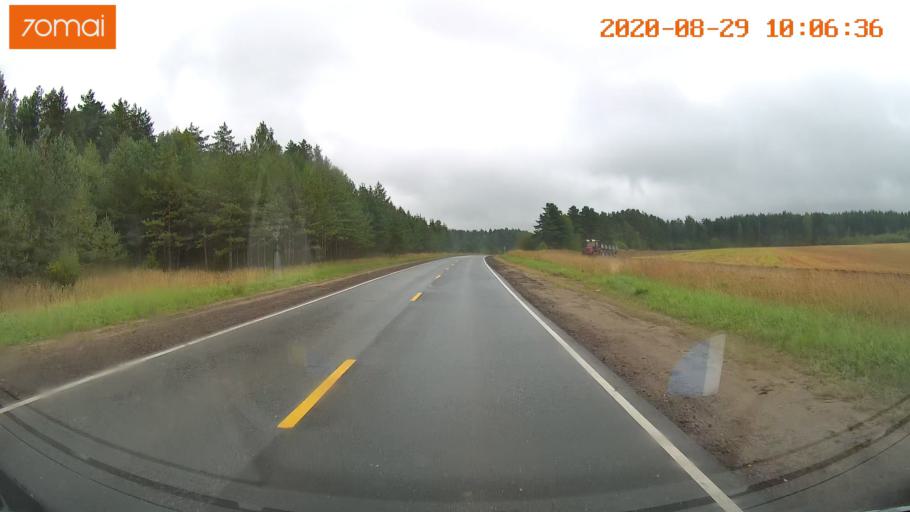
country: RU
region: Ivanovo
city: Kuznechikha
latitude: 57.3877
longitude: 42.5491
